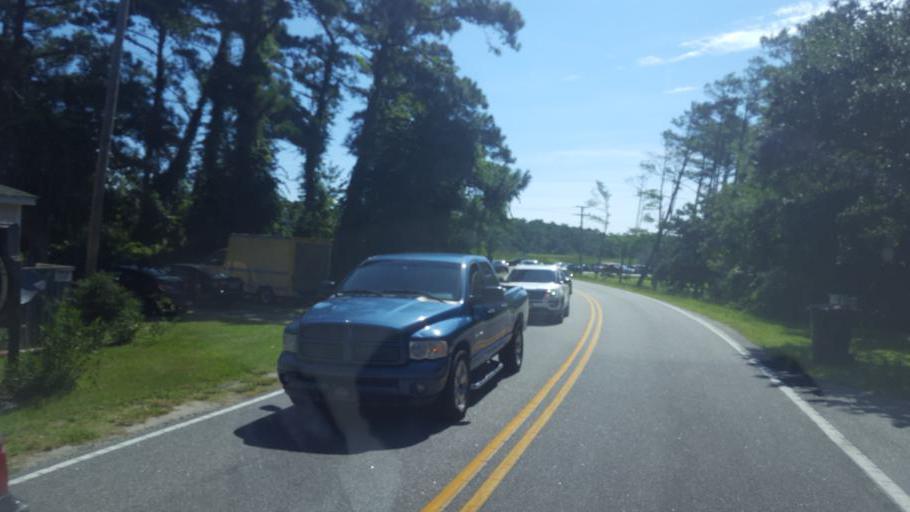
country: US
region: North Carolina
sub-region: Dare County
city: Kill Devil Hills
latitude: 36.0086
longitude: -75.7030
